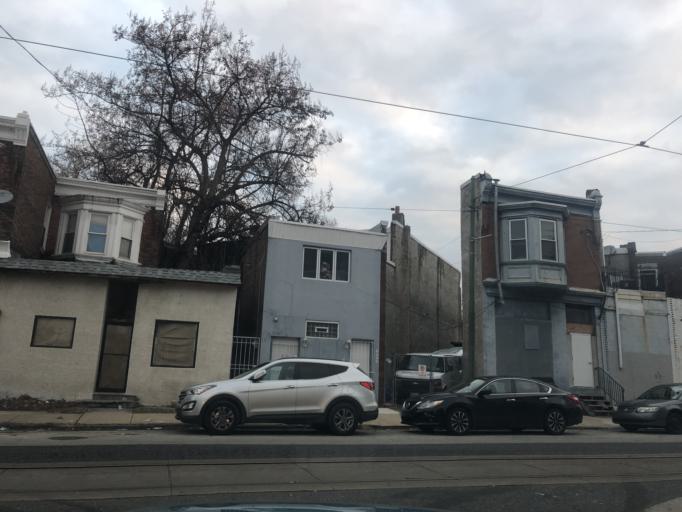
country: US
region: Pennsylvania
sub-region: Delaware County
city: Millbourne
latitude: 39.9698
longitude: -75.2402
